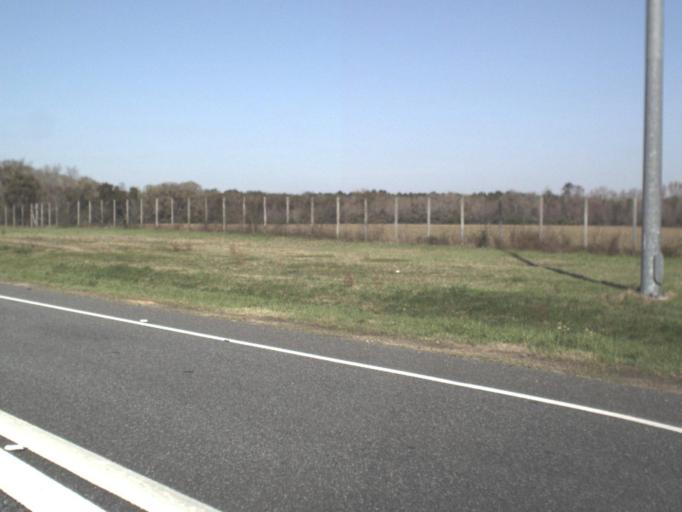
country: US
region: Florida
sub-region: Jackson County
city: Marianna
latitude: 30.7229
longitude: -85.1921
